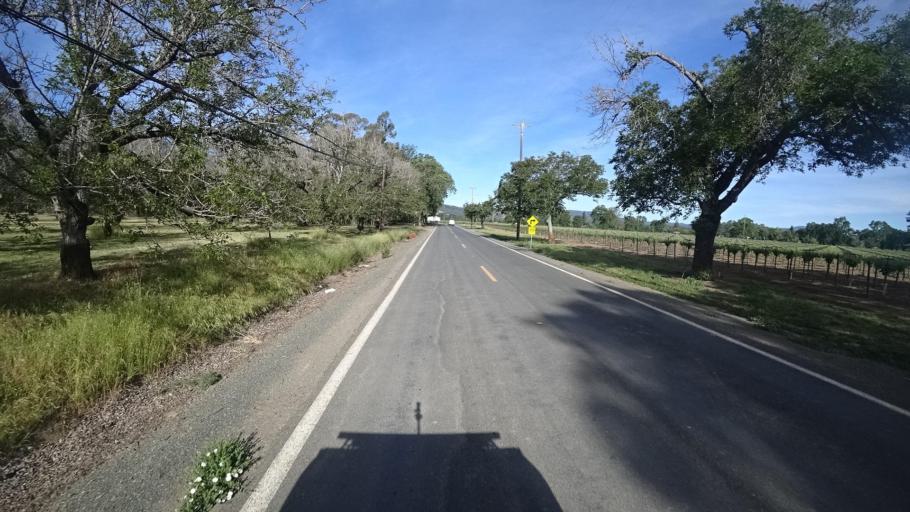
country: US
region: California
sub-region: Lake County
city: Kelseyville
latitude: 39.0037
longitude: -122.8828
